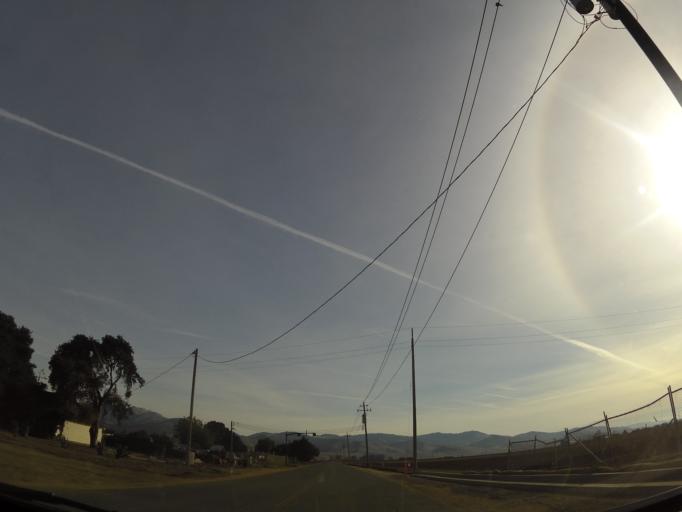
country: US
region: California
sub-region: Monterey County
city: Boronda
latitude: 36.7292
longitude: -121.6264
